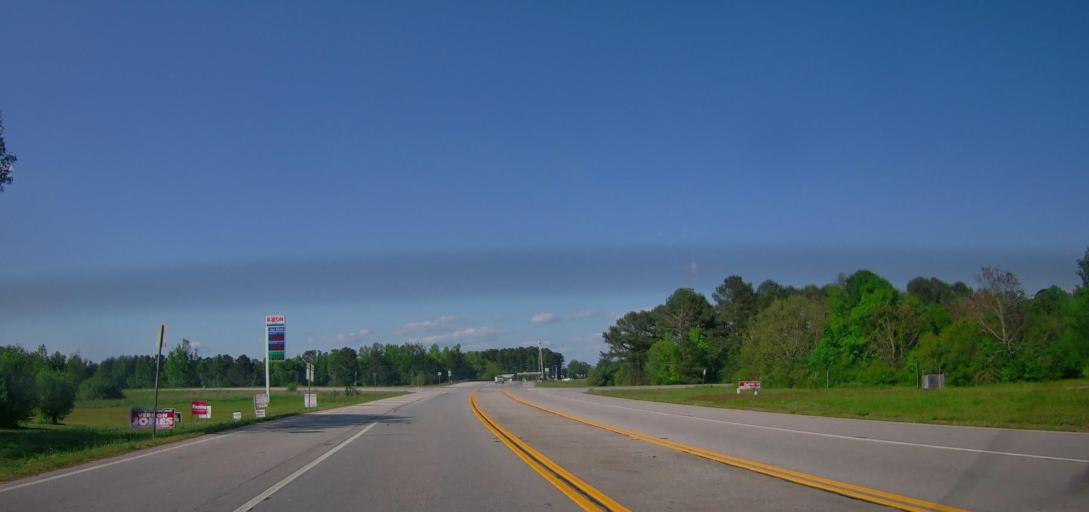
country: US
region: Georgia
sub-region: Morgan County
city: Madison
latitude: 33.5595
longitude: -83.4998
